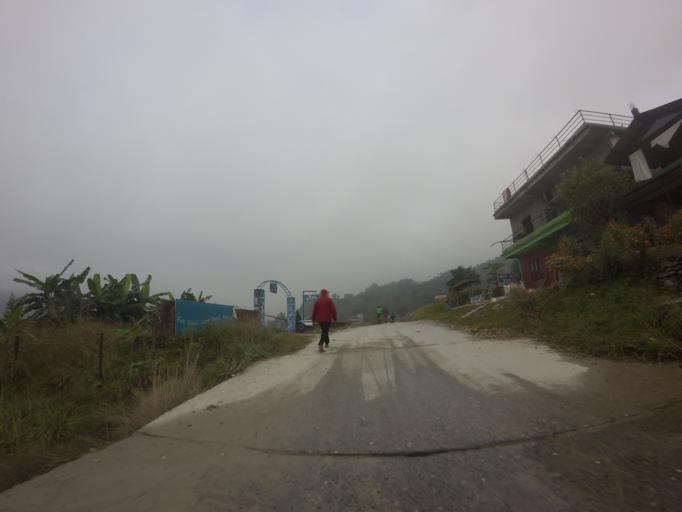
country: NP
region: Western Region
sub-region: Gandaki Zone
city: Pokhara
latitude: 28.2270
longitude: 83.9406
